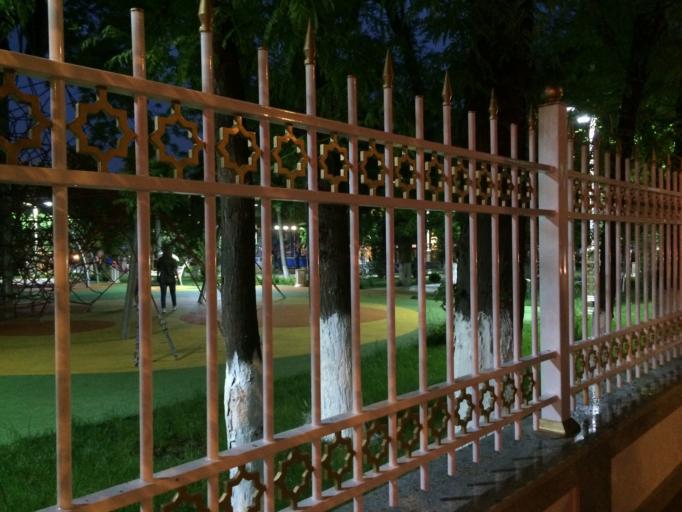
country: TM
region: Ahal
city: Ashgabat
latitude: 37.9376
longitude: 58.3907
